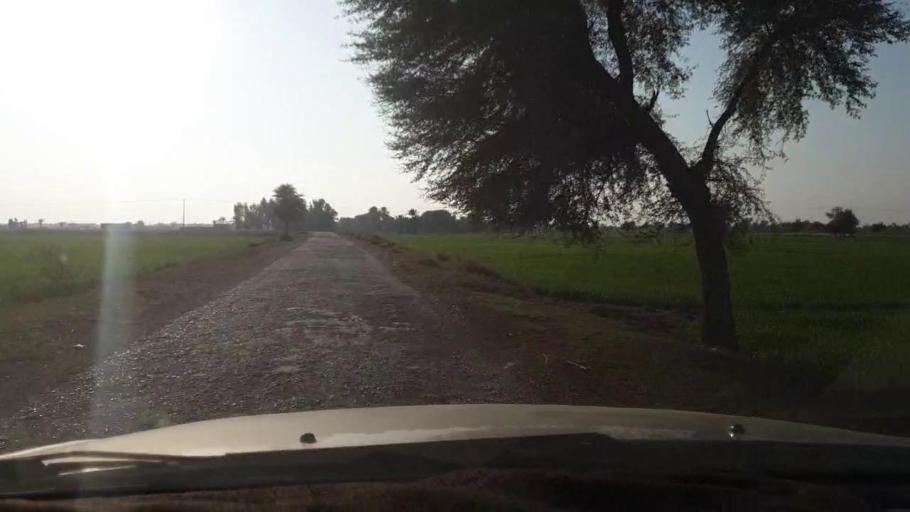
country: PK
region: Sindh
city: Mirpur Mathelo
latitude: 28.0087
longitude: 69.5367
